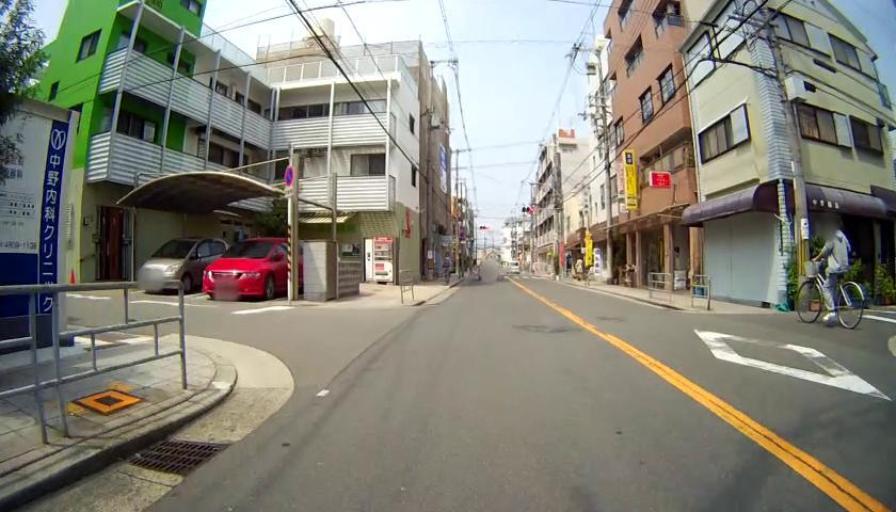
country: JP
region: Osaka
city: Suita
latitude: 34.7523
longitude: 135.5358
